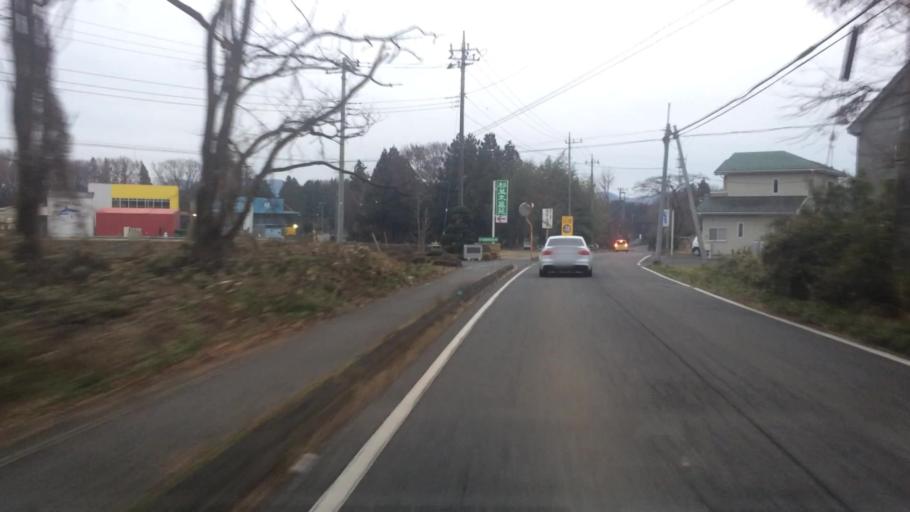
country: JP
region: Tochigi
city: Imaichi
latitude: 36.6796
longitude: 139.7692
